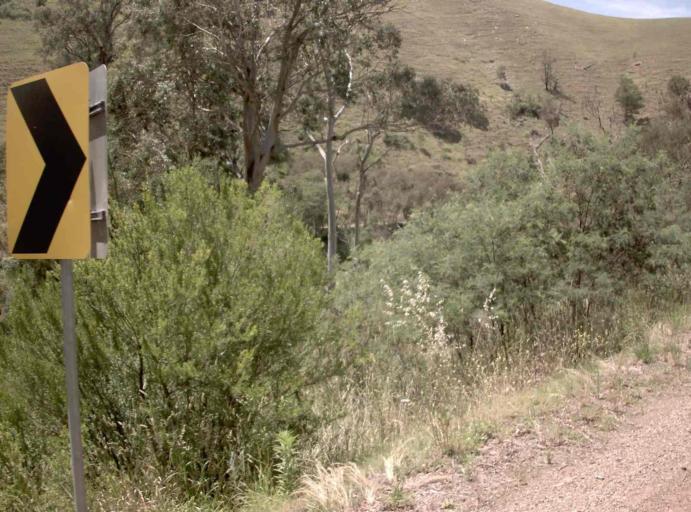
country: AU
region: Victoria
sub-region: East Gippsland
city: Bairnsdale
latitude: -37.3915
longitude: 147.8361
